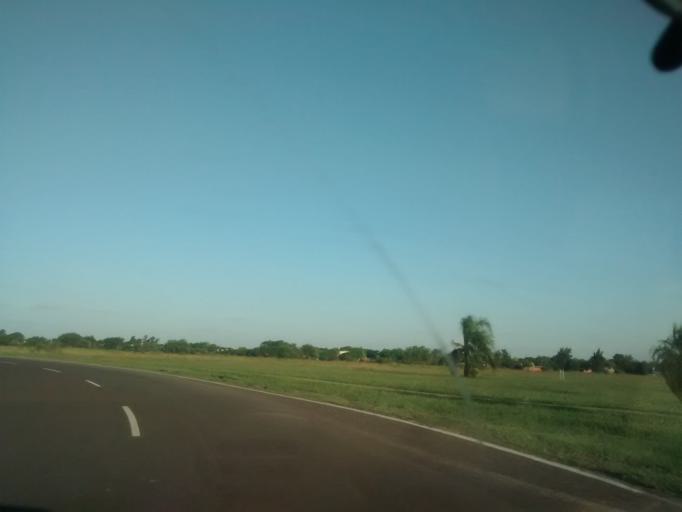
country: AR
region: Chaco
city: Fontana
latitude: -27.4446
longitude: -59.0428
